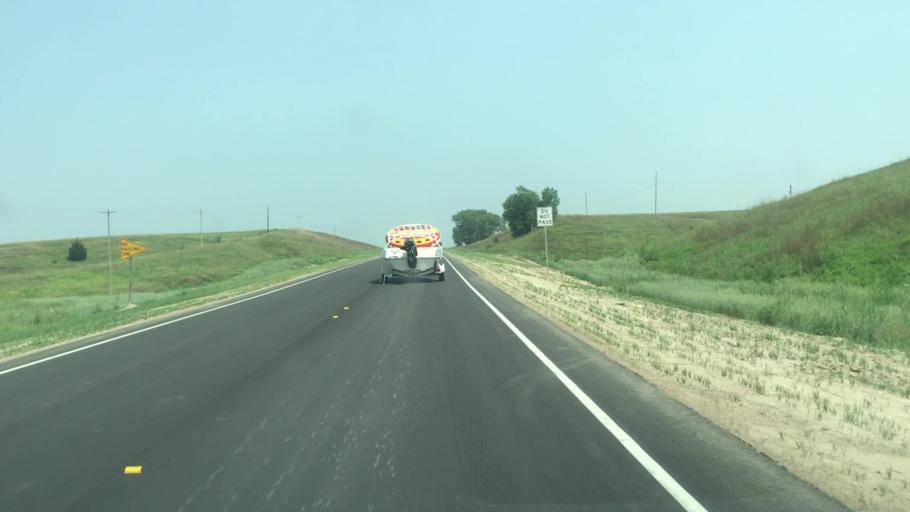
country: US
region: Nebraska
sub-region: Sherman County
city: Loup City
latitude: 41.2630
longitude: -98.9333
